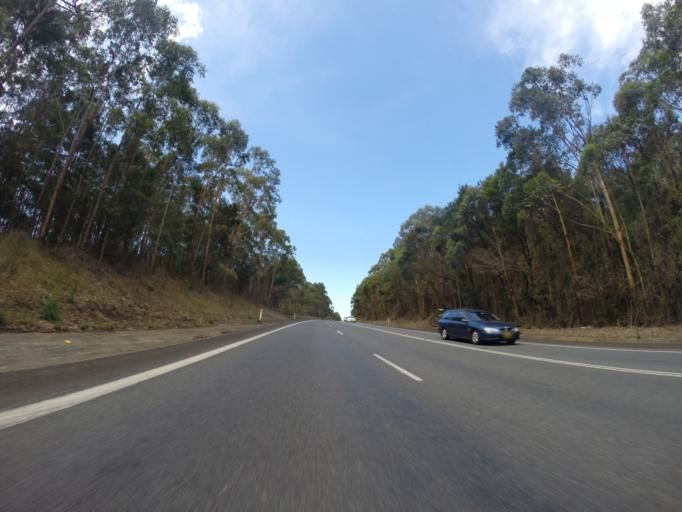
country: AU
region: New South Wales
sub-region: Shoalhaven Shire
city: Falls Creek
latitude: -35.0439
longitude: 150.5780
